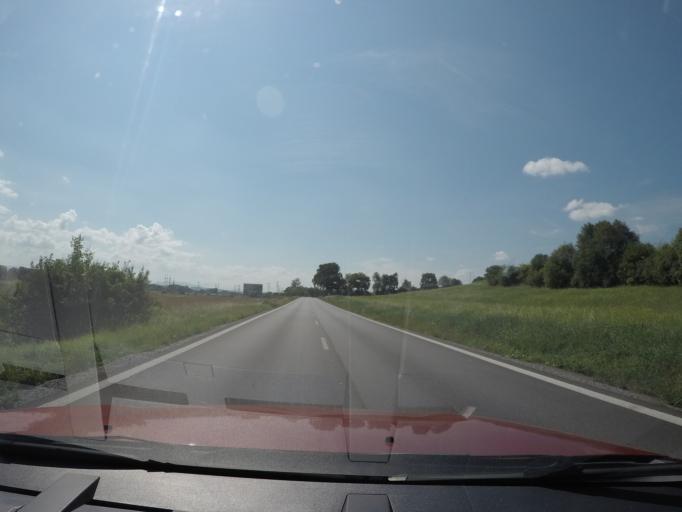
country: SK
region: Presovsky
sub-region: Okres Presov
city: Presov
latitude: 48.8697
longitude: 21.2523
